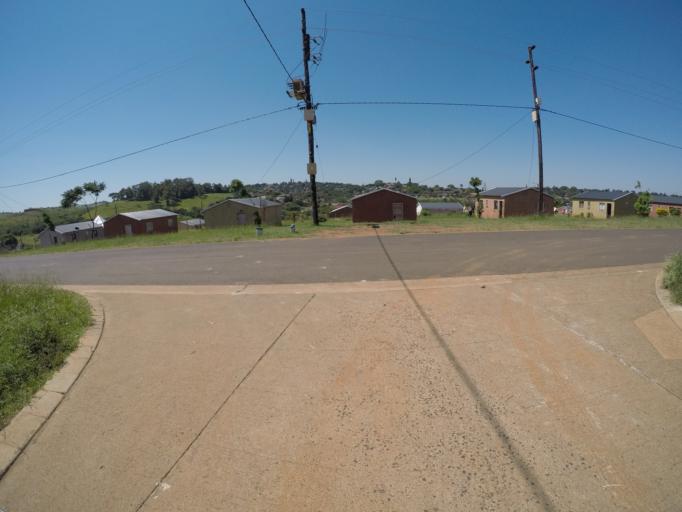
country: ZA
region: KwaZulu-Natal
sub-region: uThungulu District Municipality
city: Empangeni
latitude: -28.7647
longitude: 31.8808
